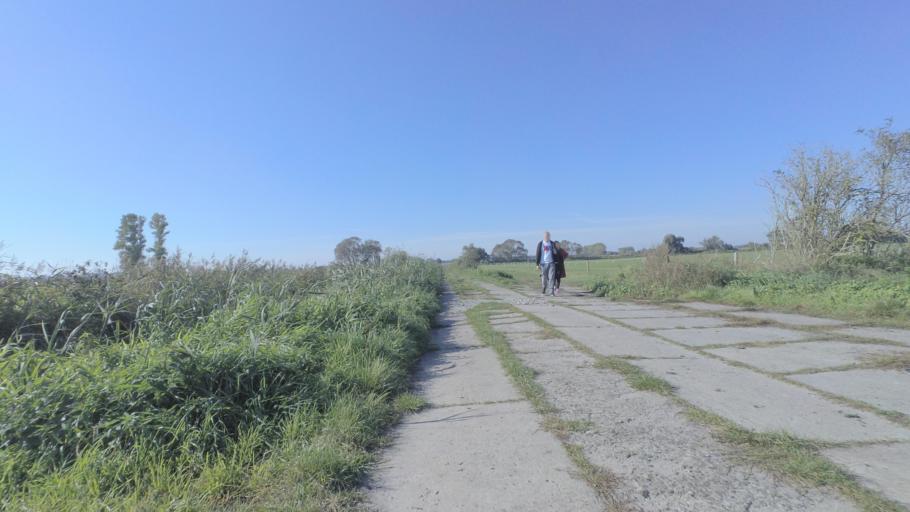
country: DE
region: Brandenburg
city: Rangsdorf
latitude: 52.3033
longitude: 13.3619
